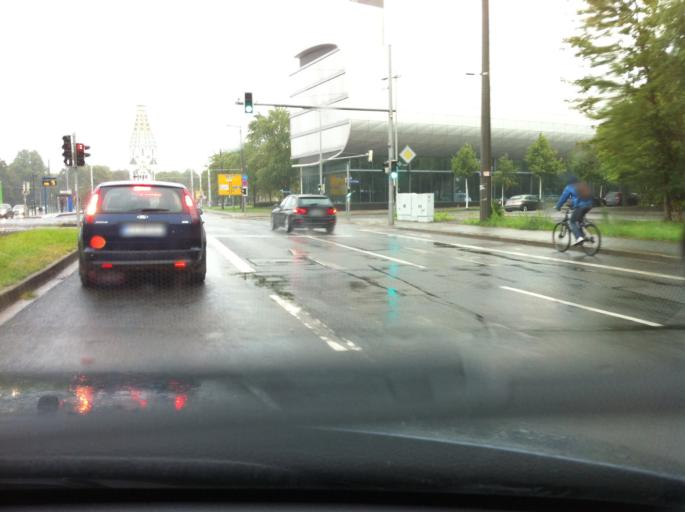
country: DE
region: Saxony
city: Leipzig
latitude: 51.3226
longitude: 12.3929
